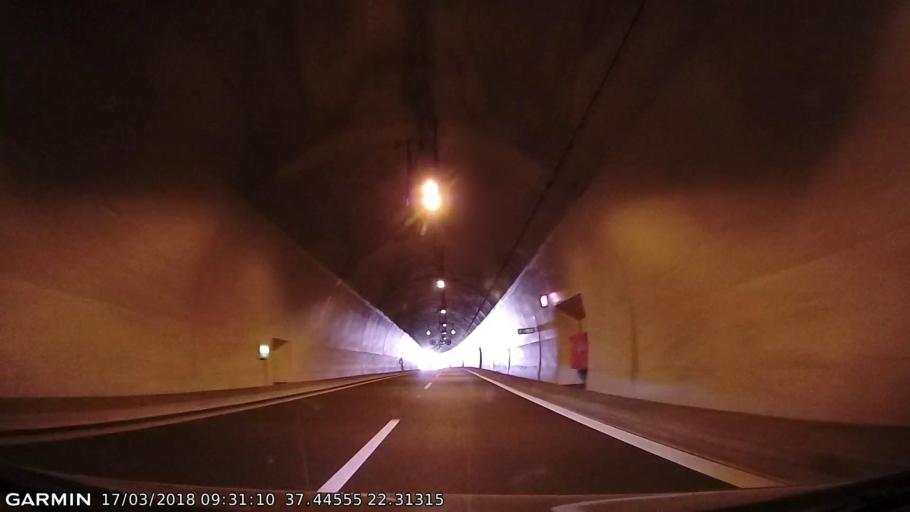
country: GR
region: Peloponnese
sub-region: Nomos Arkadias
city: Tripoli
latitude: 37.4454
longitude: 22.3128
